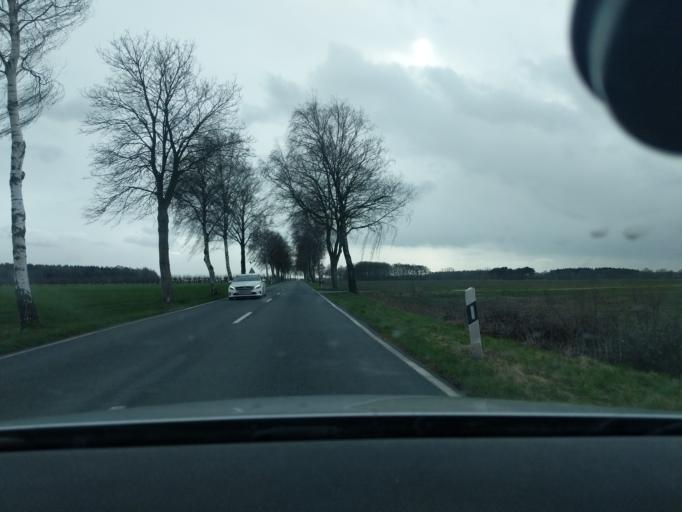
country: DE
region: Lower Saxony
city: Bliedersdorf
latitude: 53.5013
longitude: 9.5393
